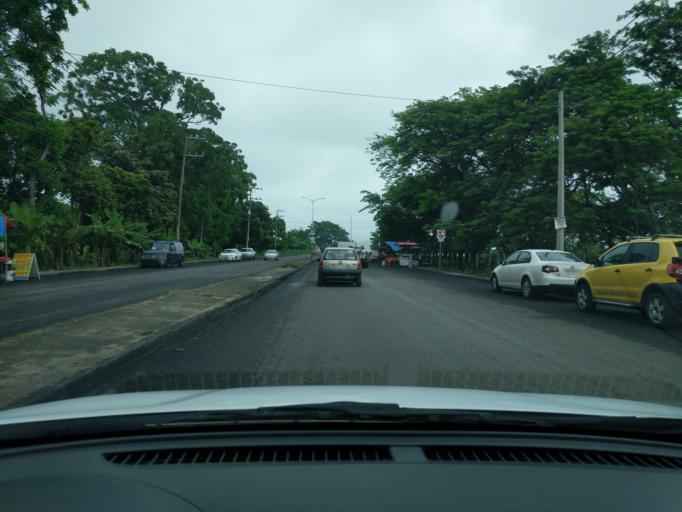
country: MX
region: Tabasco
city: Villahermosa
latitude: 17.9616
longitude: -92.9641
